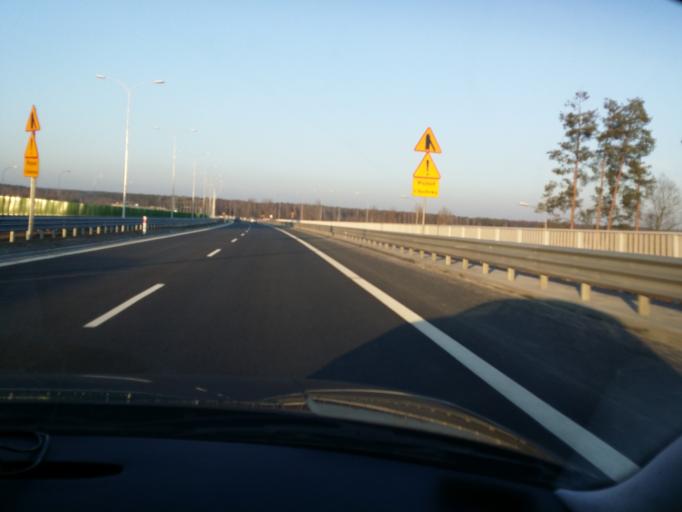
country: PL
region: Swietokrzyskie
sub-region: Powiat skarzyski
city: Skarzysko-Kamienna
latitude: 51.1591
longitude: 20.8536
